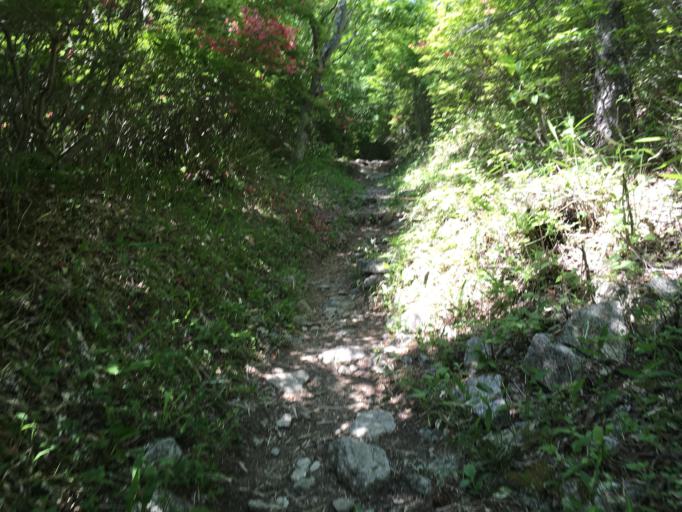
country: JP
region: Iwate
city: Ofunato
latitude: 39.1795
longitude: 141.7409
